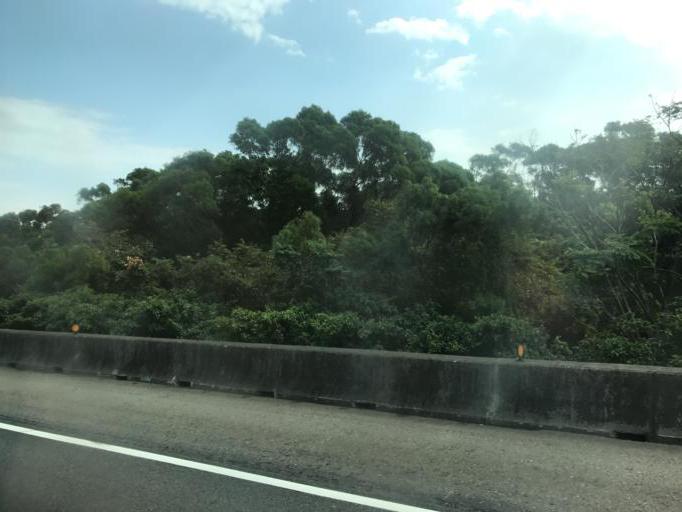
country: TW
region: Taiwan
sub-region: Hsinchu
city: Zhubei
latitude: 24.8770
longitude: 121.0413
